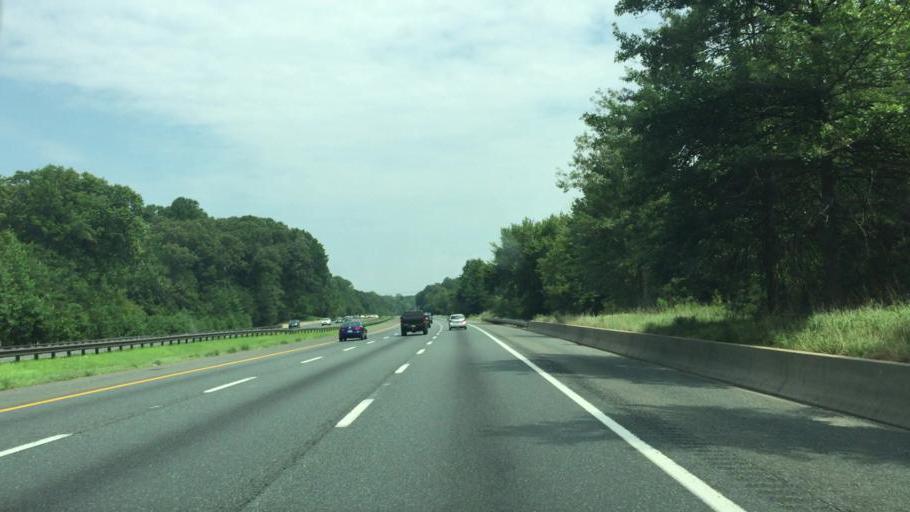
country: US
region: Maryland
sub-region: Anne Arundel County
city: Davidsonville
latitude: 38.9687
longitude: -76.6263
